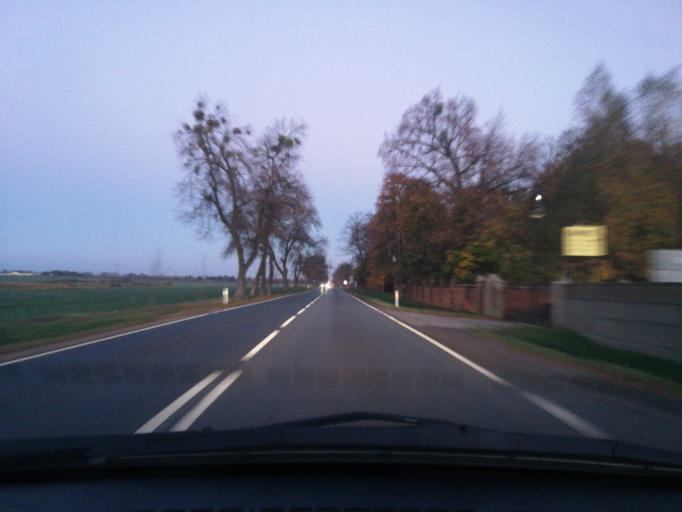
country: PL
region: Lodz Voivodeship
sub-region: Powiat brzezinski
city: Rogow
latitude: 51.8074
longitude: 19.8531
